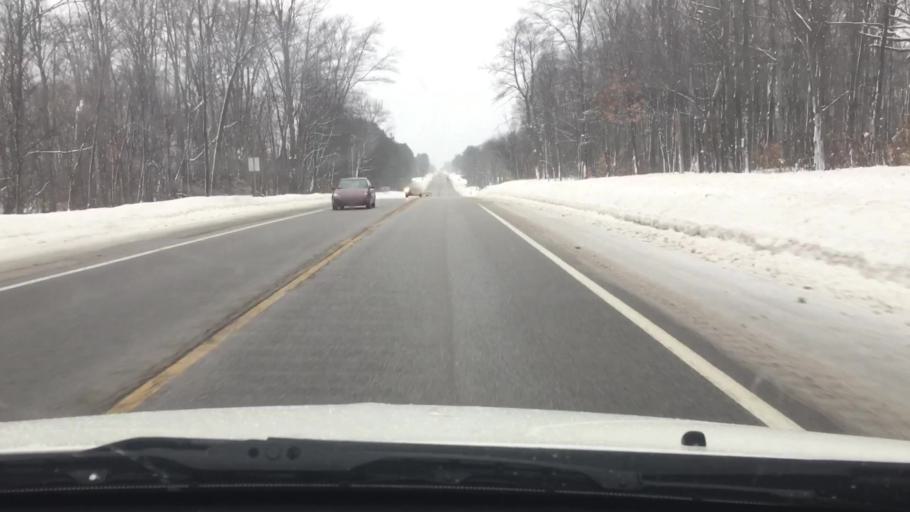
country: US
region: Michigan
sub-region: Otsego County
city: Gaylord
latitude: 45.0365
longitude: -84.7758
